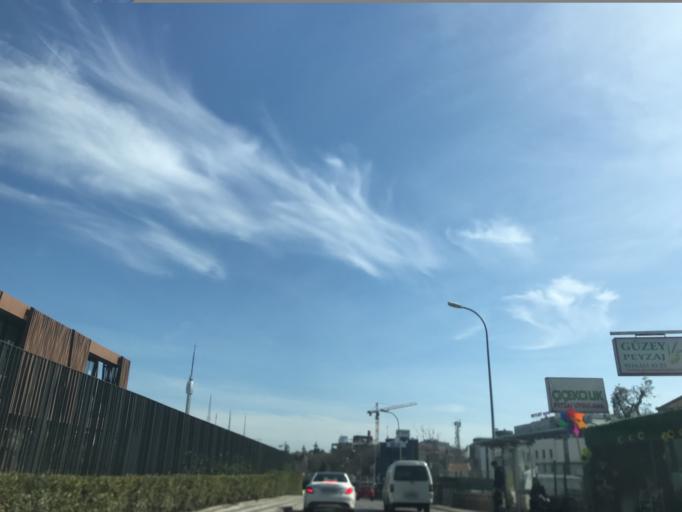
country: TR
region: Istanbul
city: UEskuedar
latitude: 41.0265
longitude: 29.0406
